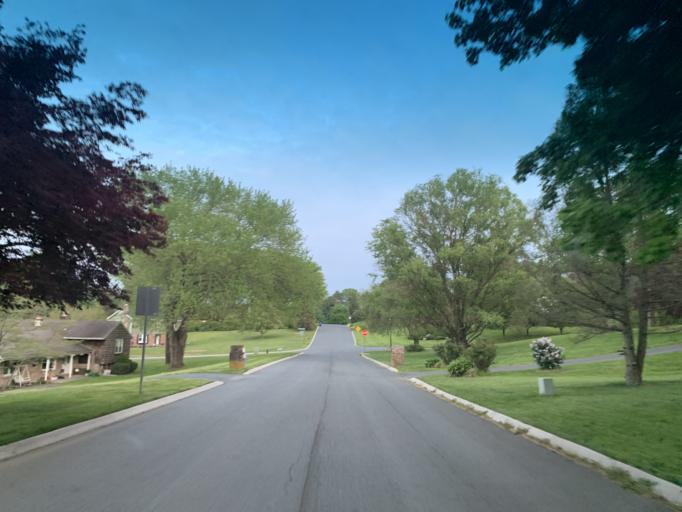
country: US
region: Maryland
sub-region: Harford County
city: South Bel Air
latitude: 39.5884
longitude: -76.2805
